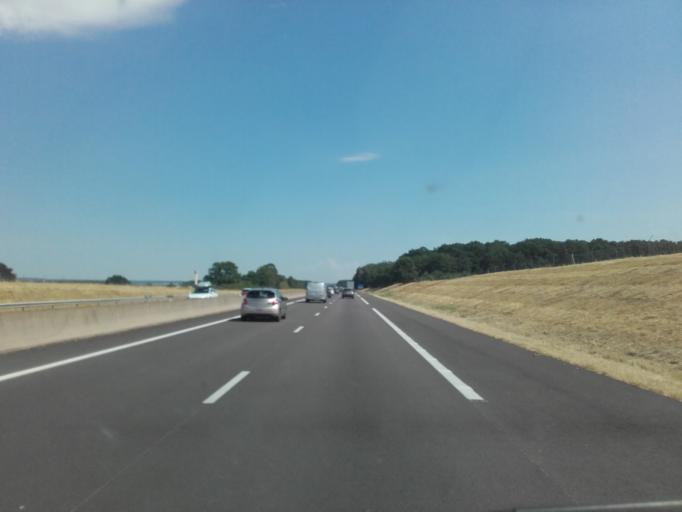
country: FR
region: Bourgogne
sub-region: Departement de la Cote-d'Or
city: Semur-en-Auxois
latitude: 47.3750
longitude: 4.3896
